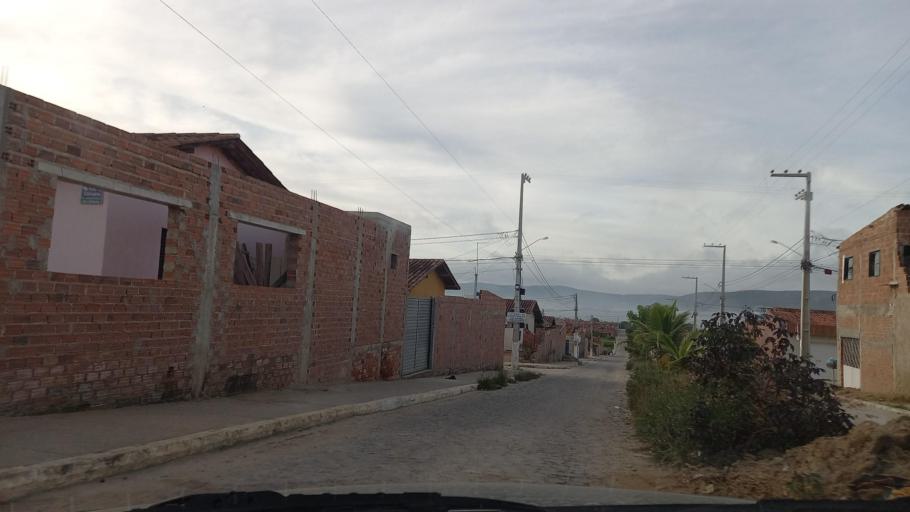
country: BR
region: Pernambuco
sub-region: Bezerros
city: Bezerros
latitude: -8.2145
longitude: -35.7415
